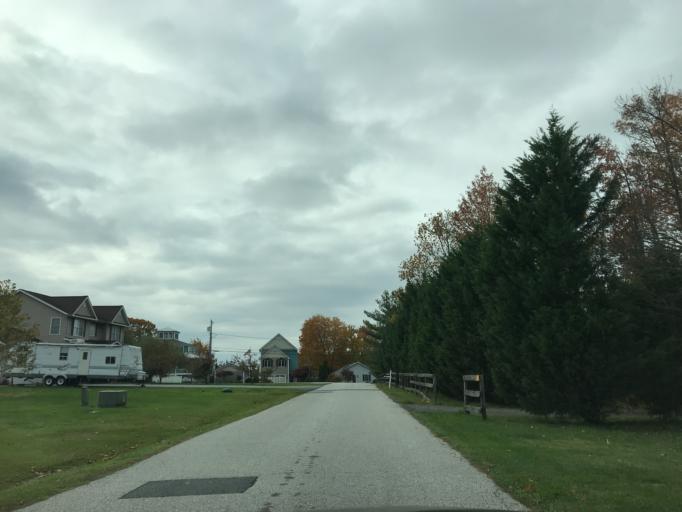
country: US
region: Maryland
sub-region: Baltimore County
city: Bowleys Quarters
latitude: 39.3205
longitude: -76.3986
